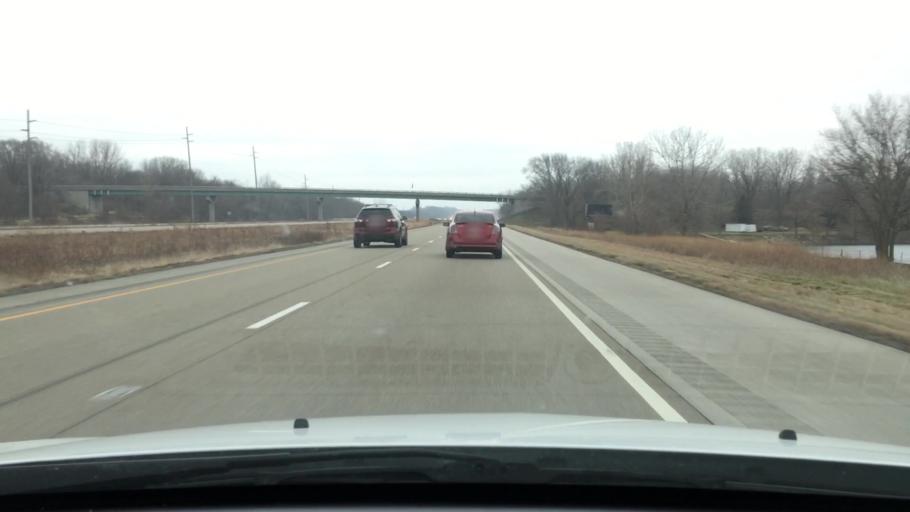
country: US
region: Illinois
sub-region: Logan County
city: Atlanta
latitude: 40.2184
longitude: -89.2803
